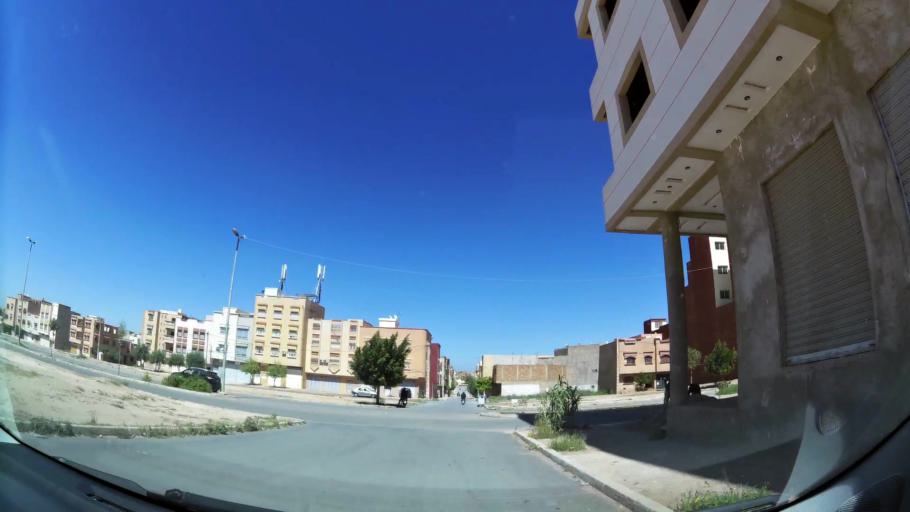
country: MA
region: Oriental
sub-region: Oujda-Angad
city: Oujda
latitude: 34.6631
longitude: -1.8743
